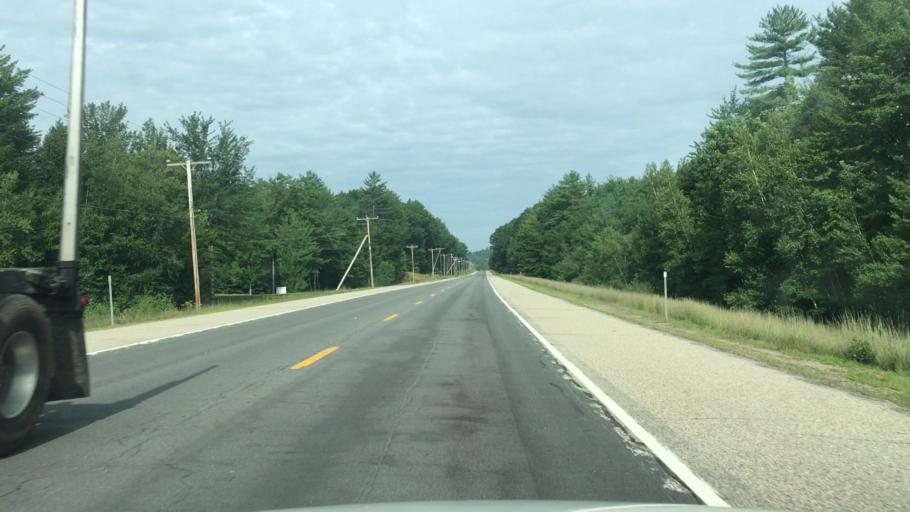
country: US
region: New Hampshire
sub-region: Carroll County
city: Tamworth
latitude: 43.8266
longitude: -71.2533
